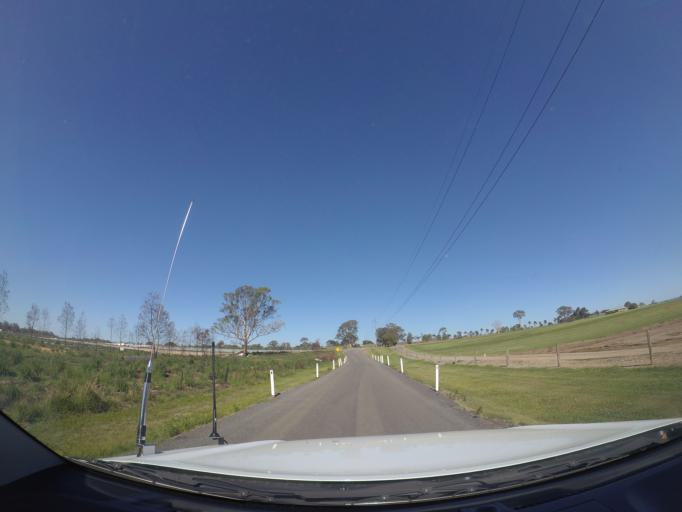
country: AU
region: Queensland
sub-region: Logan
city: Chambers Flat
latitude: -27.7620
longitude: 153.0819
